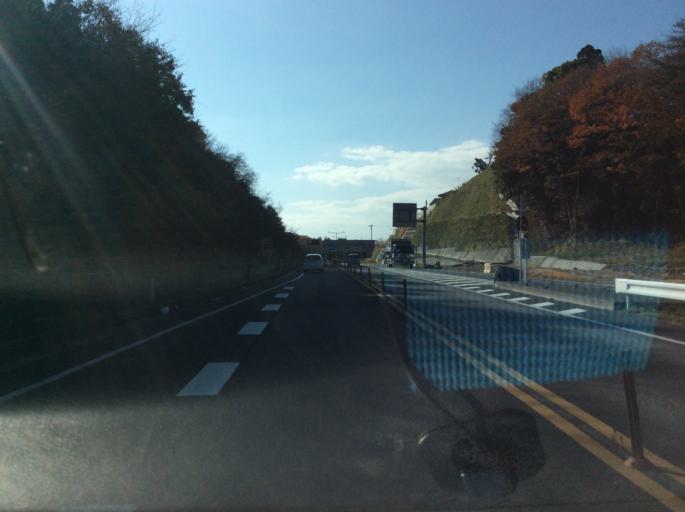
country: JP
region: Fukushima
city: Iwaki
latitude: 37.0339
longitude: 140.9130
